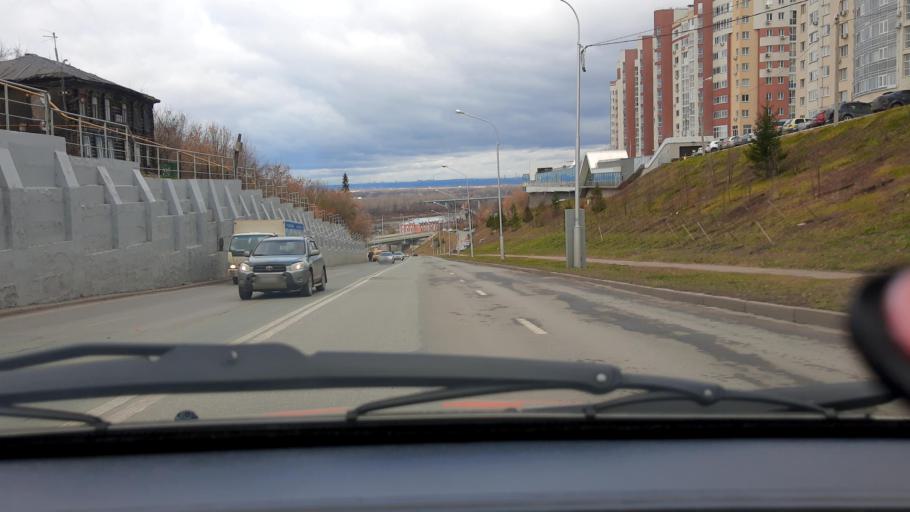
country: RU
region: Bashkortostan
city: Ufa
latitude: 54.7448
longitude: 55.9514
